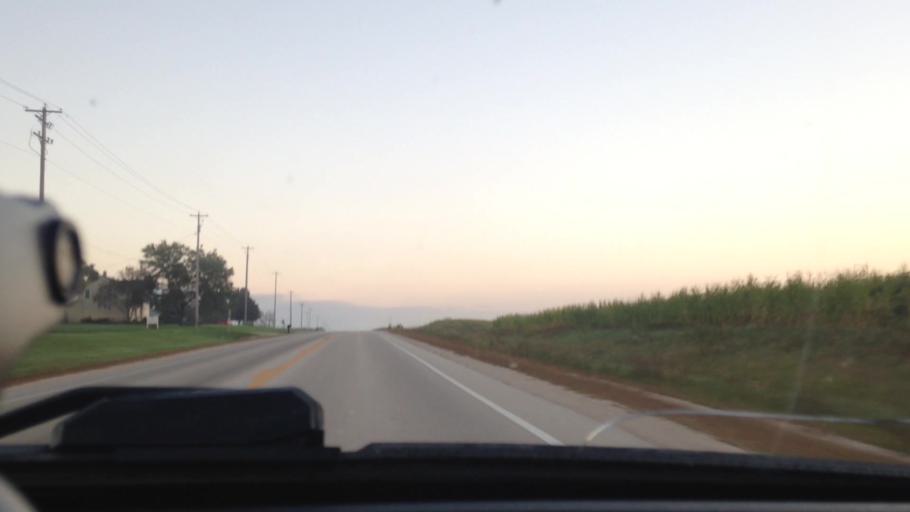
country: US
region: Wisconsin
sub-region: Dodge County
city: Lomira
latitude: 43.5718
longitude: -88.4497
